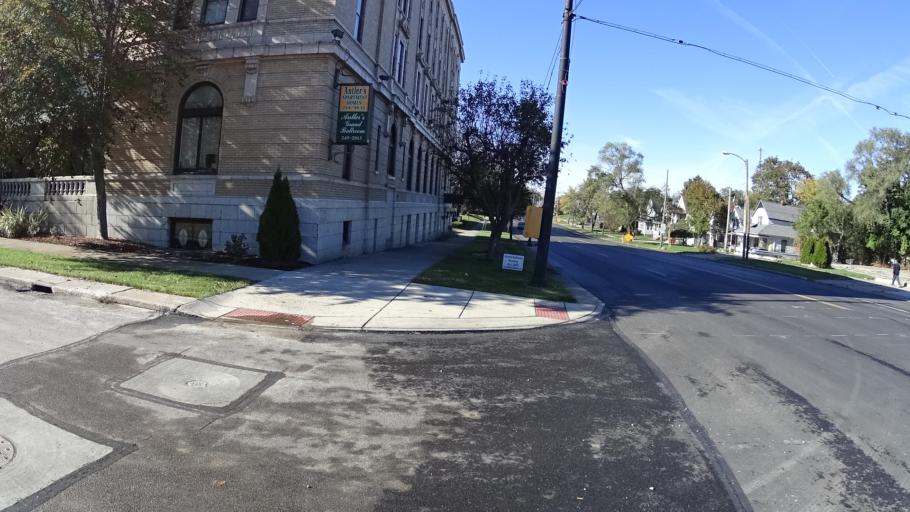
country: US
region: Ohio
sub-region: Lorain County
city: Lorain
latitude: 41.4676
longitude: -82.1806
